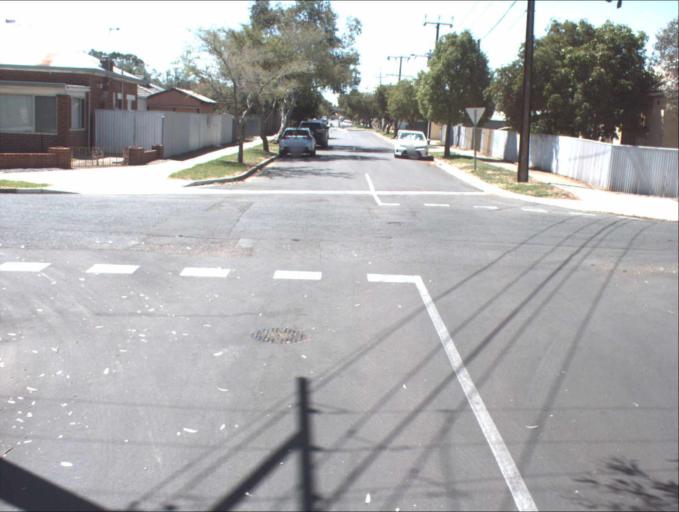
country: AU
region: South Australia
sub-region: Port Adelaide Enfield
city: Enfield
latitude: -34.8615
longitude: 138.6172
